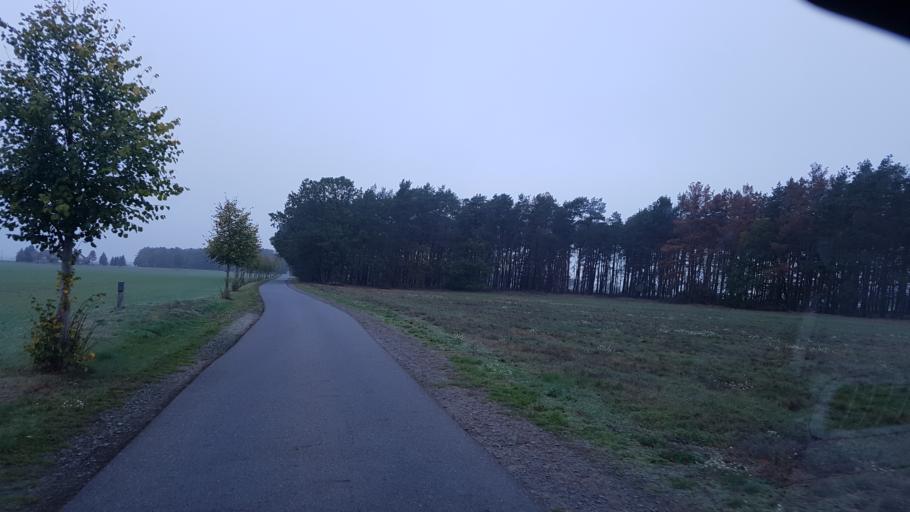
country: DE
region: Brandenburg
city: Sonnewalde
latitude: 51.6725
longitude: 13.6349
